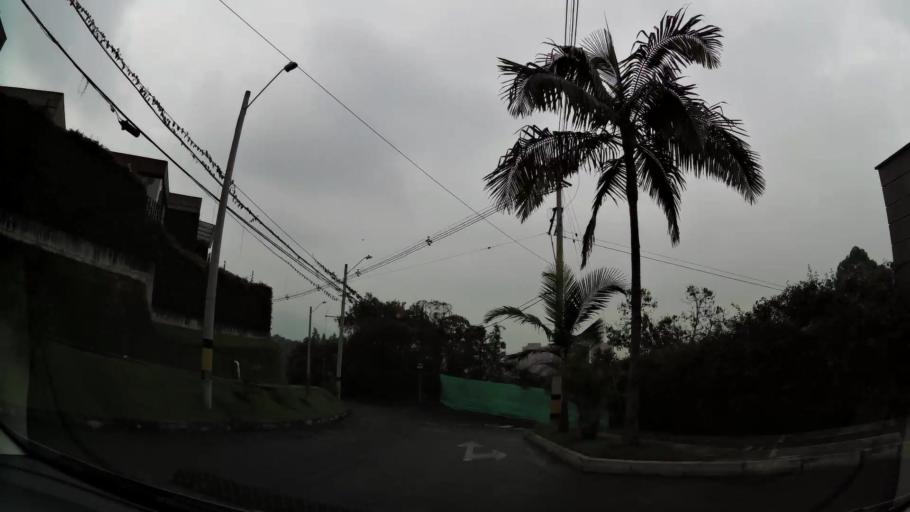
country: CO
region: Antioquia
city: Envigado
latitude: 6.1731
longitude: -75.5633
